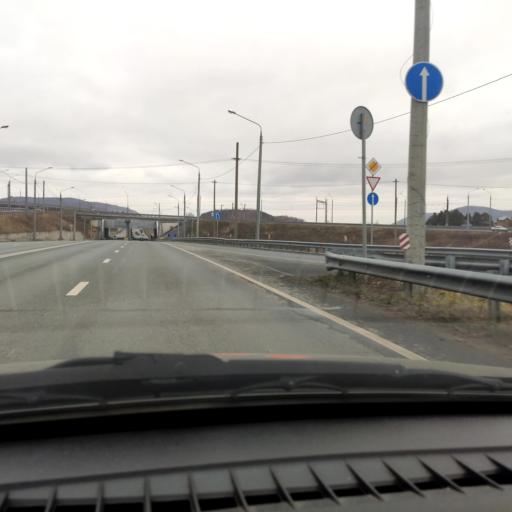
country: RU
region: Samara
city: Volzhskiy
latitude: 53.4358
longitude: 50.1131
